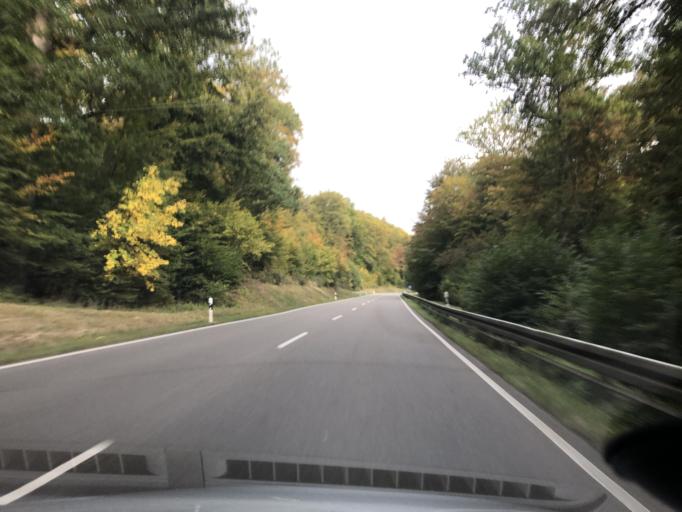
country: DE
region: Baden-Wuerttemberg
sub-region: Regierungsbezirk Stuttgart
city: Gerlingen
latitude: 48.7605
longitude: 9.0624
